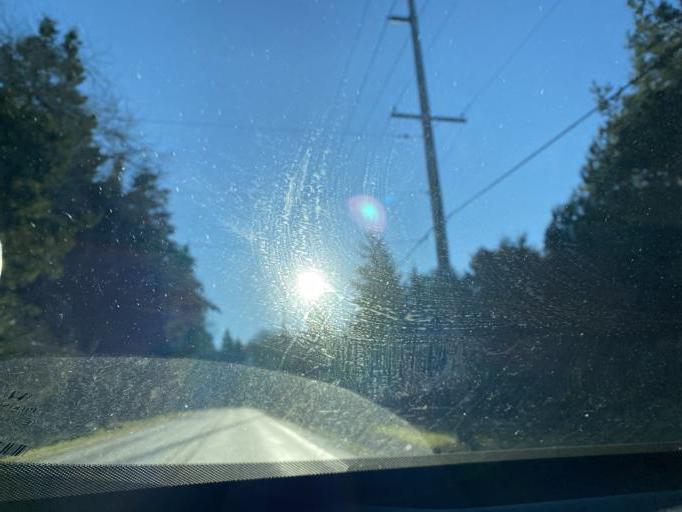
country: US
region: Washington
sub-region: Island County
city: Camano
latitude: 48.1033
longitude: -122.5744
